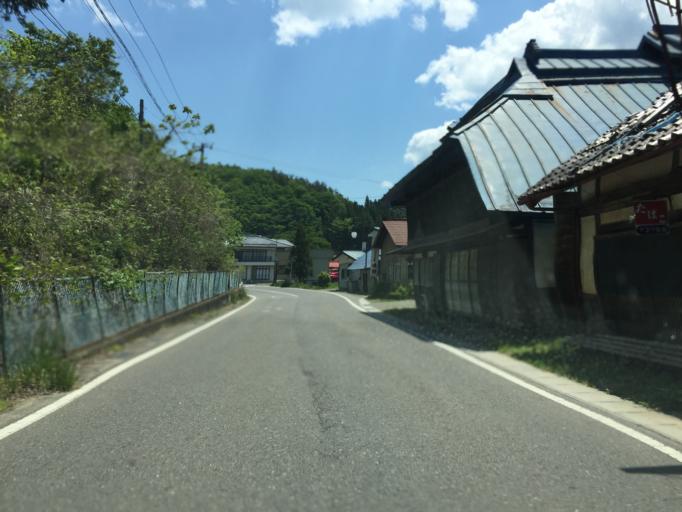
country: JP
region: Fukushima
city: Funehikimachi-funehiki
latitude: 37.5132
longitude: 140.6618
